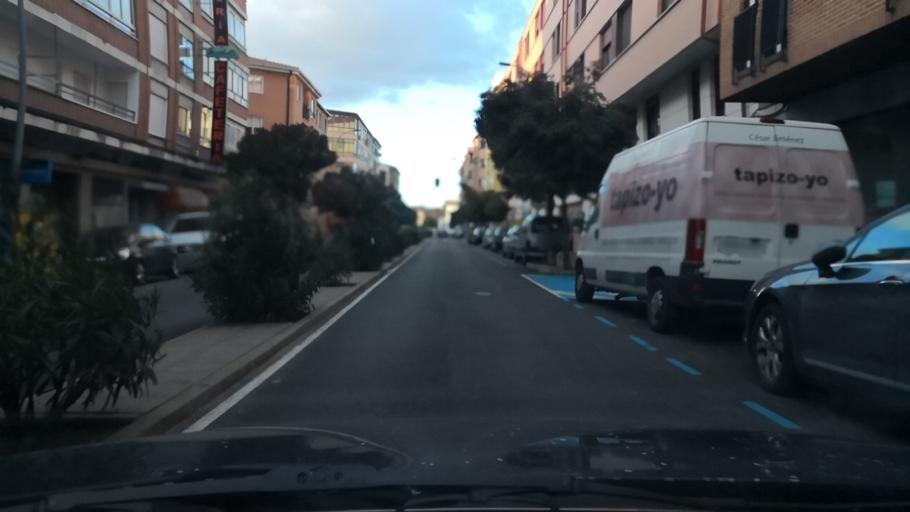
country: ES
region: Castille and Leon
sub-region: Provincia de Valladolid
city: Medina del Campo
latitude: 41.3074
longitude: -4.9116
